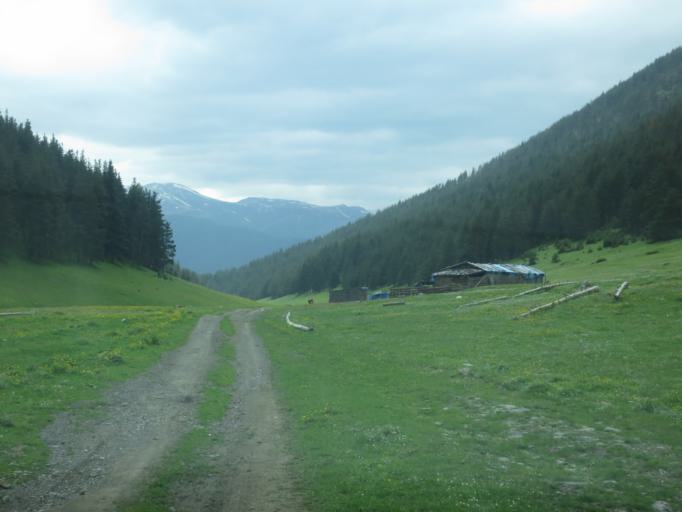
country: RU
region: Chechnya
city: Itum-Kali
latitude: 42.3902
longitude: 45.6772
